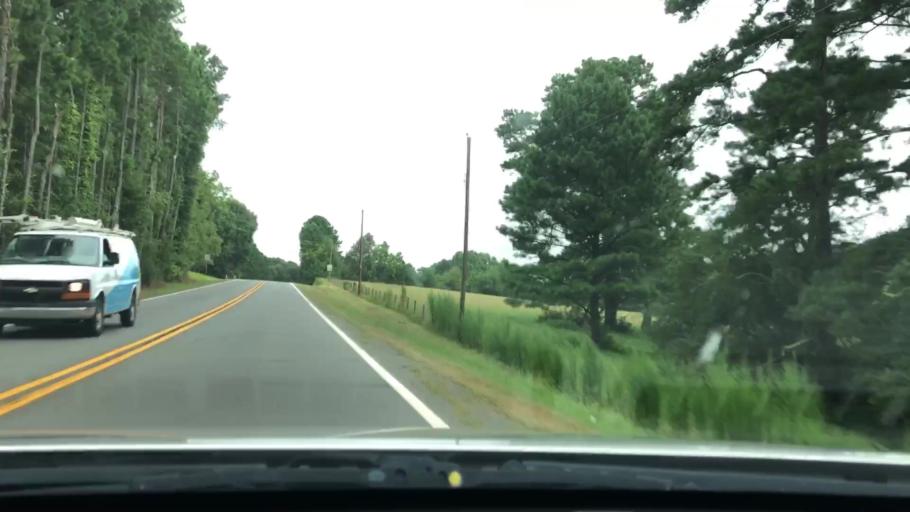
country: US
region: Georgia
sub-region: Upson County
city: Hannahs Mill
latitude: 33.0181
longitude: -84.4976
